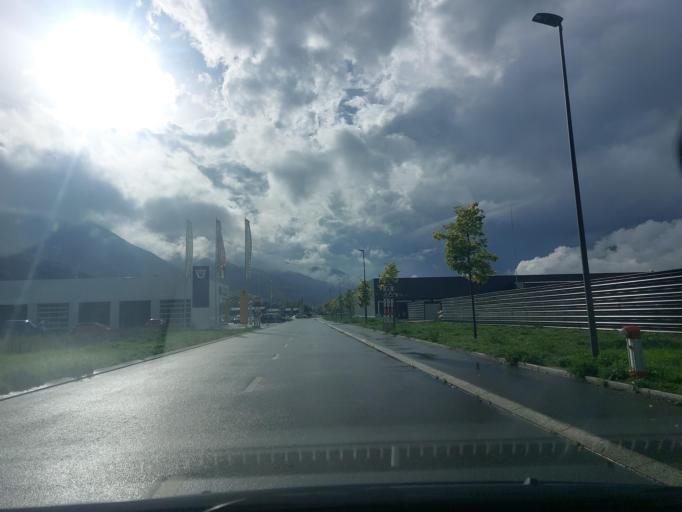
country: CH
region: Valais
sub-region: Sierre District
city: Chalais
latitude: 46.2737
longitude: 7.5211
